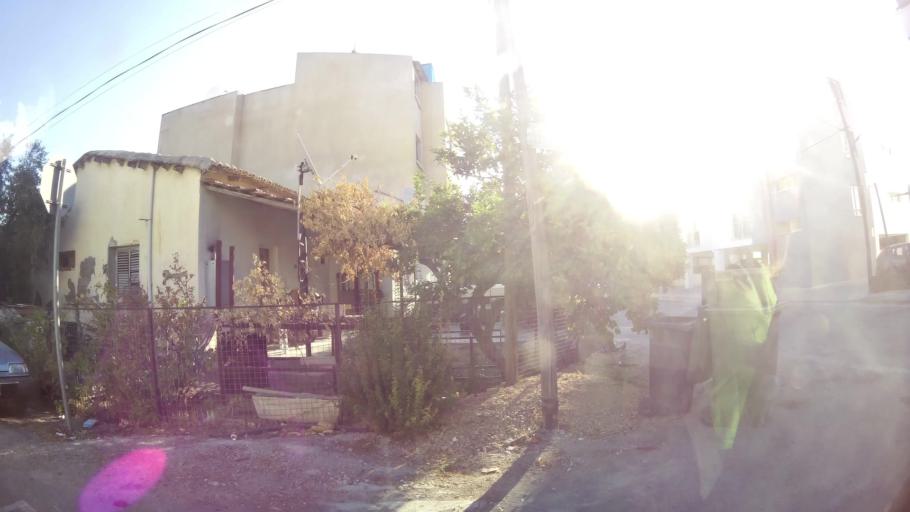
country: CY
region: Lefkosia
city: Nicosia
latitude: 35.2029
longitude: 33.3439
